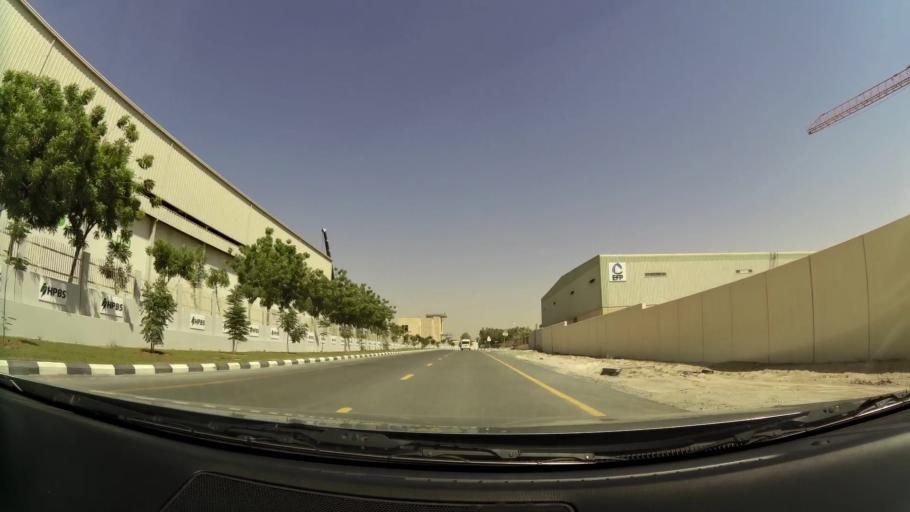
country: AE
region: Dubai
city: Dubai
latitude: 24.9715
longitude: 55.1784
